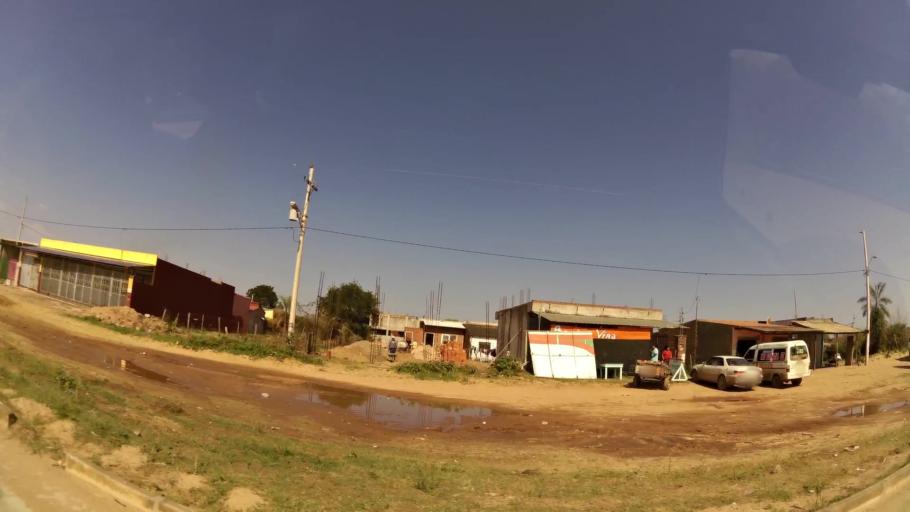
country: BO
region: Santa Cruz
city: Cotoca
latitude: -17.7165
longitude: -63.0706
